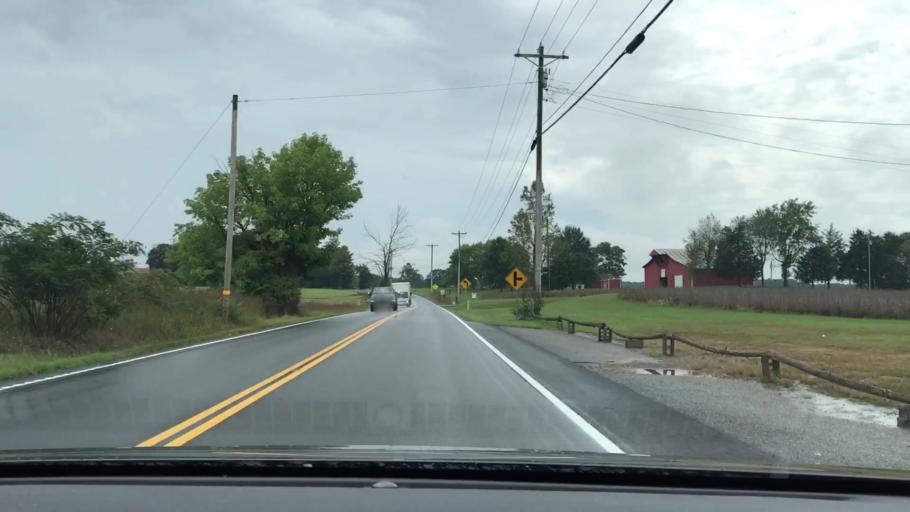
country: US
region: Tennessee
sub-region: Macon County
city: Red Boiling Springs
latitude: 36.5029
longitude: -85.8662
